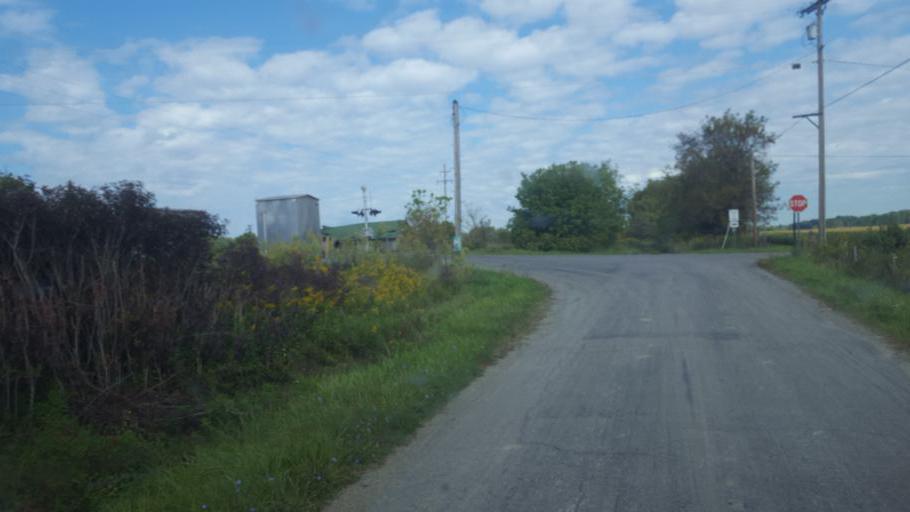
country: US
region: Pennsylvania
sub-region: Mercer County
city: Greenville
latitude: 41.5117
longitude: -80.3655
